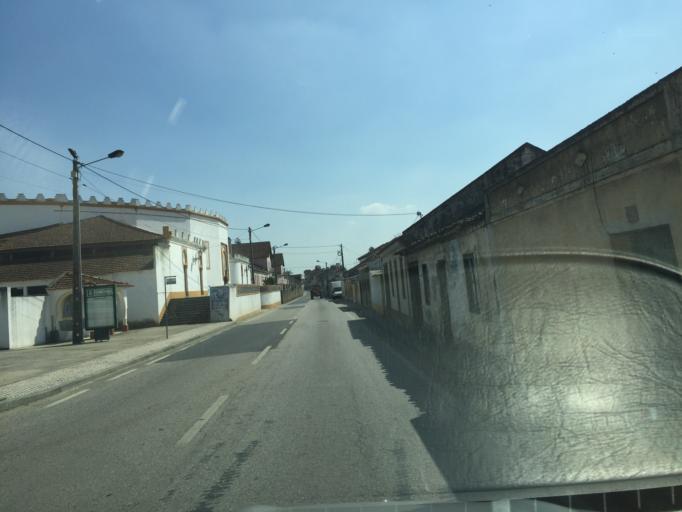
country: PT
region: Santarem
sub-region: Golega
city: Golega
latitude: 39.3630
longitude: -8.4783
